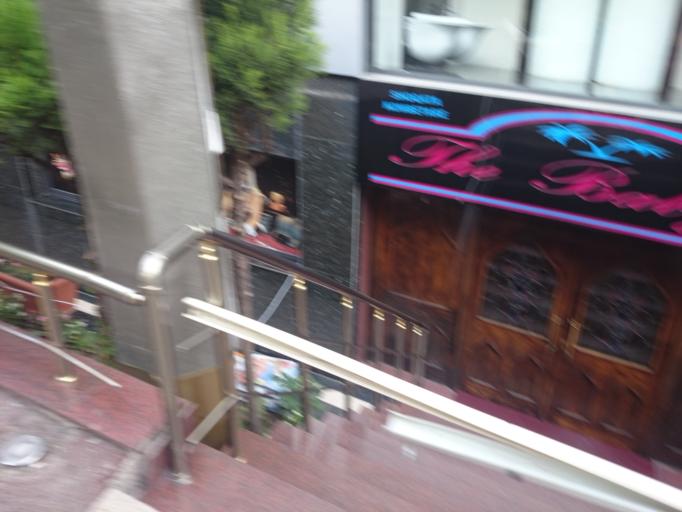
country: AL
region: Tirane
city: Tirana
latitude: 41.3207
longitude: 19.8141
